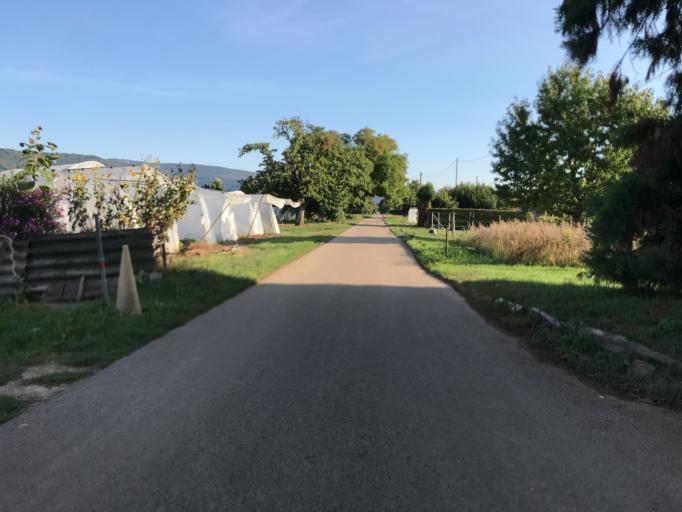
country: DE
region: Baden-Wuerttemberg
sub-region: Karlsruhe Region
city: Dossenheim
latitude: 49.4378
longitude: 8.6662
